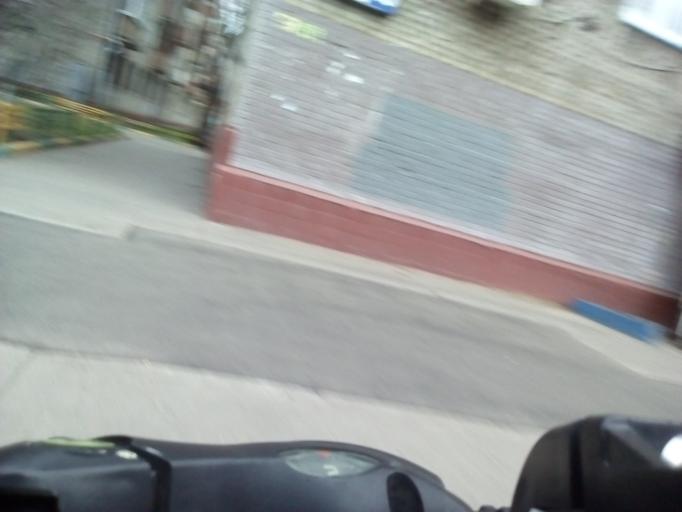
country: RU
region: Moscow
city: Lefortovo
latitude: 55.7593
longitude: 37.7165
